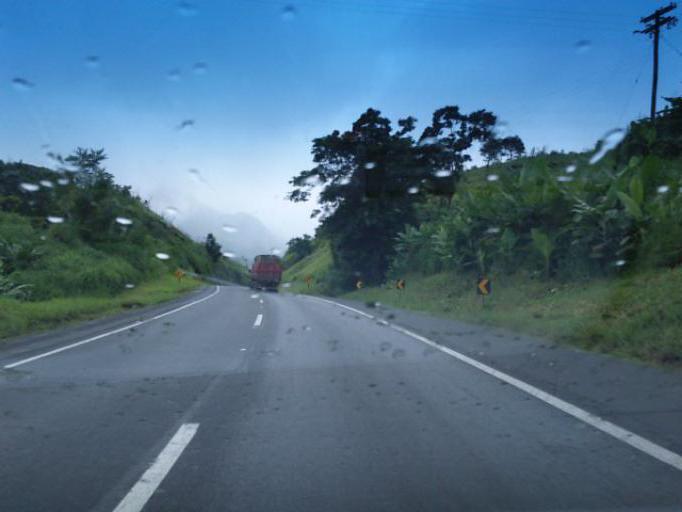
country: BR
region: Sao Paulo
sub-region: Cajati
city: Cajati
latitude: -24.7844
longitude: -48.1886
